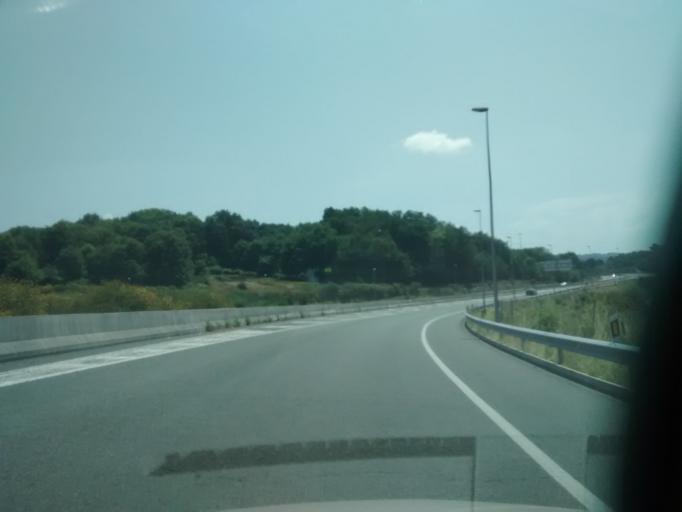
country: ES
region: Galicia
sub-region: Provincia de Ourense
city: Maside
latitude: 42.4066
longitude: -8.0124
